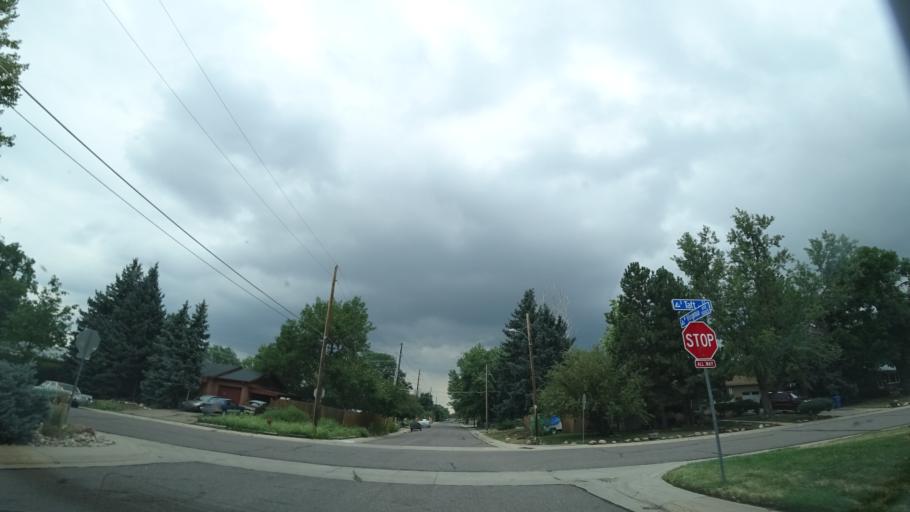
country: US
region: Colorado
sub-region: Jefferson County
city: Lakewood
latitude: 39.7074
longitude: -105.1306
